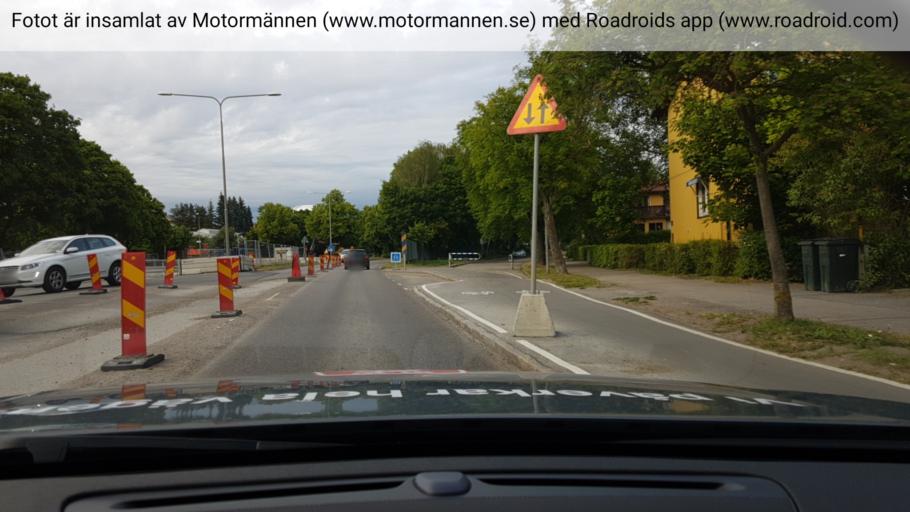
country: SE
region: Stockholm
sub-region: Stockholms Kommun
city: Arsta
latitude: 59.2841
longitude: 18.0735
